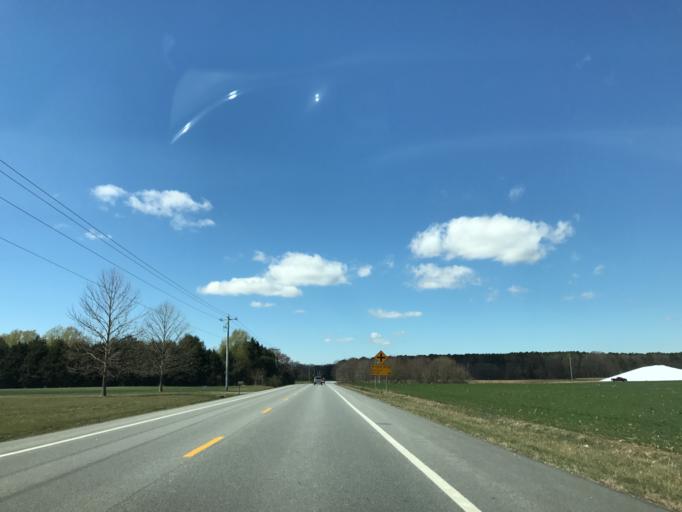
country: US
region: Maryland
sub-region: Caroline County
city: Ridgely
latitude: 39.1124
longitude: -75.9086
